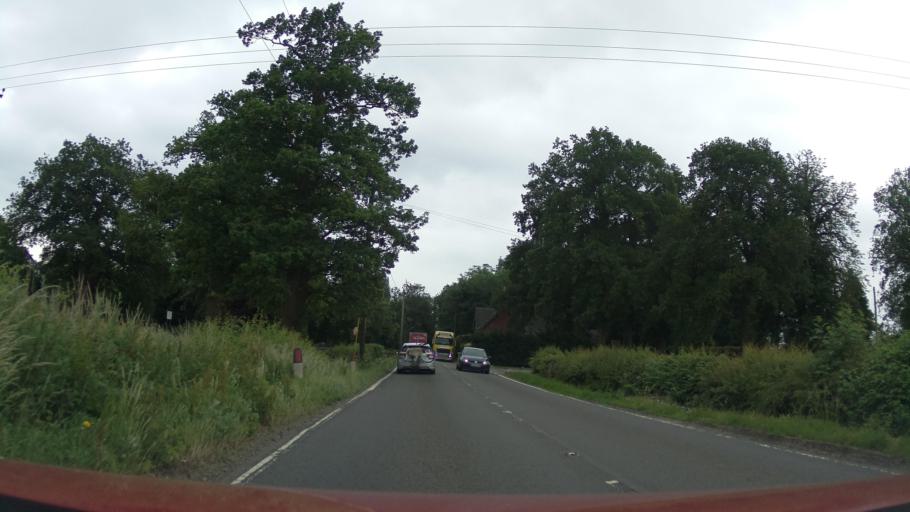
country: GB
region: England
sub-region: Derbyshire
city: Rodsley
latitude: 52.9010
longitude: -1.7666
